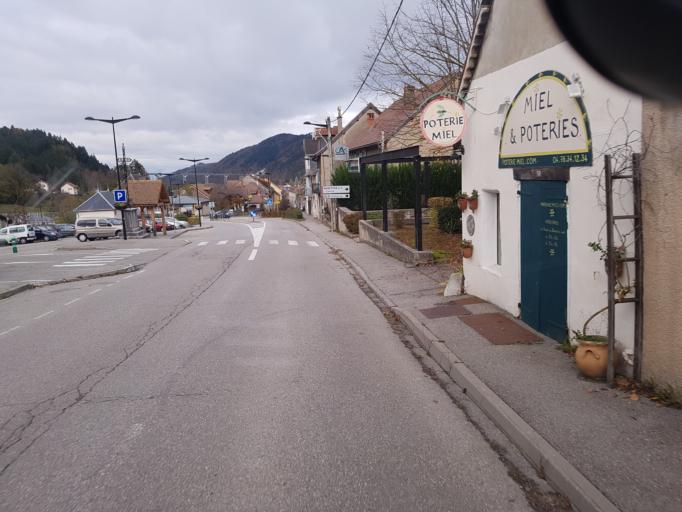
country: FR
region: Rhone-Alpes
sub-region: Departement de l'Isere
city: La Motte-Saint-Martin
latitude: 44.9152
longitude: 5.6342
